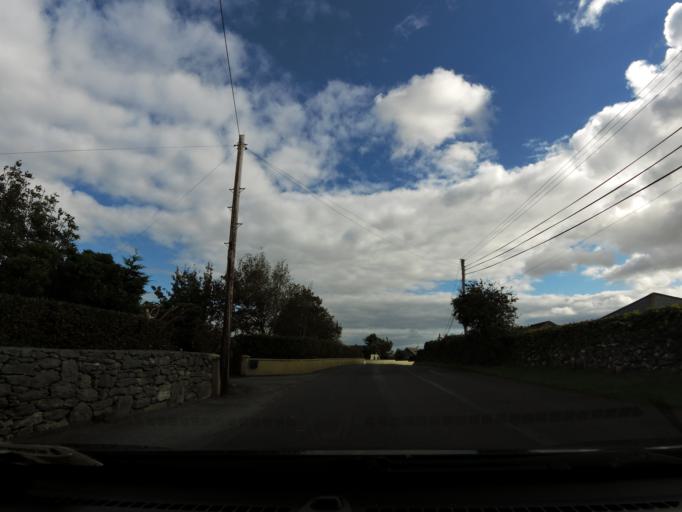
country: IE
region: Connaught
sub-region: County Galway
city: Moycullen
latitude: 53.3482
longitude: -9.1728
